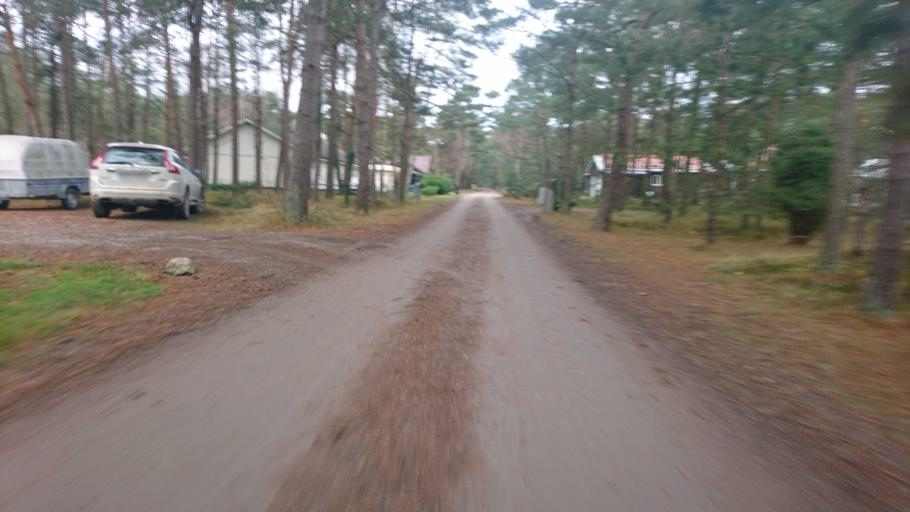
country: SE
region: Skane
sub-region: Vellinge Kommun
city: Ljunghusen
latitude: 55.3910
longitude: 12.9159
